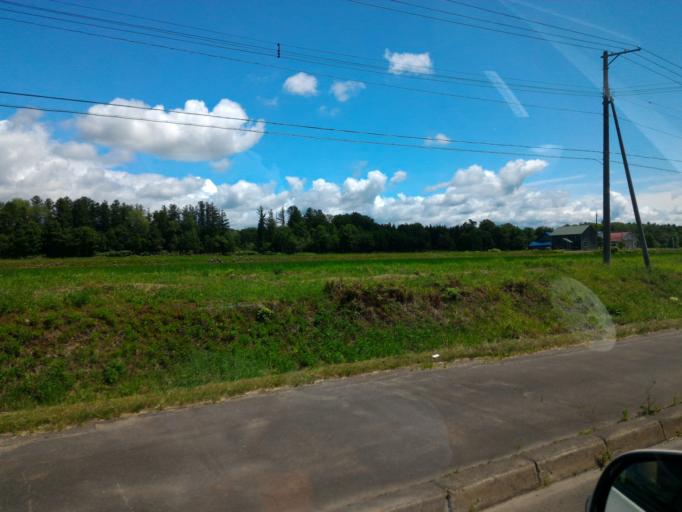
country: JP
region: Hokkaido
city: Nayoro
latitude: 44.5087
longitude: 142.3335
